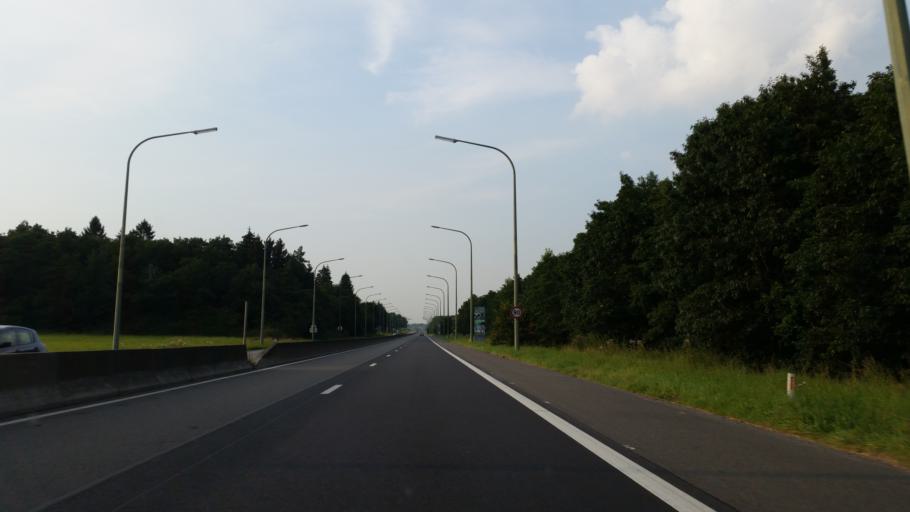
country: BE
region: Wallonia
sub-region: Province du Luxembourg
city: Marche-en-Famenne
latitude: 50.2682
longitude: 5.3474
